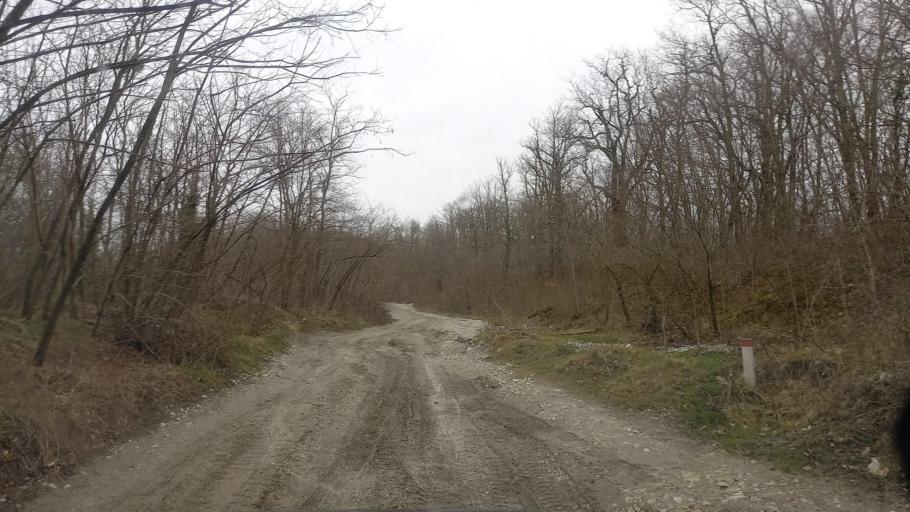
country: RU
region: Krasnodarskiy
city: Divnomorskoye
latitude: 44.5458
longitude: 38.2353
